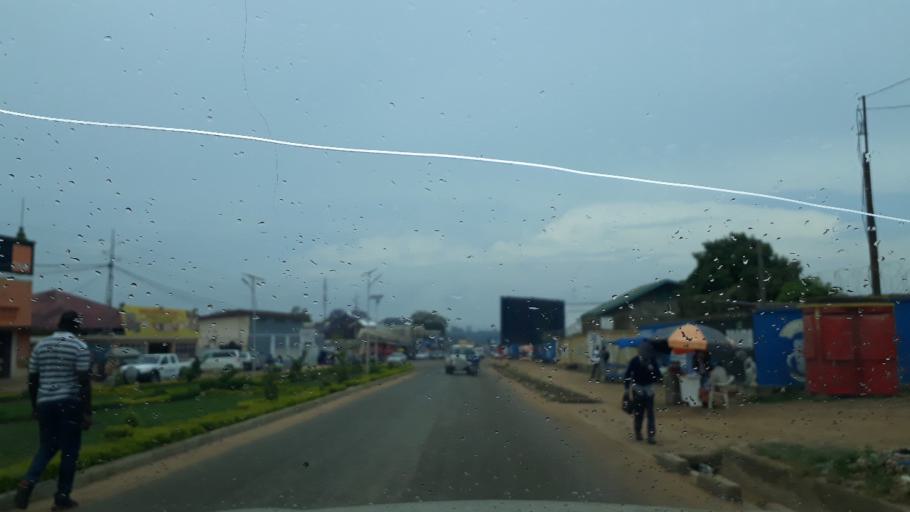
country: CD
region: Eastern Province
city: Bunia
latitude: 1.5627
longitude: 30.2488
